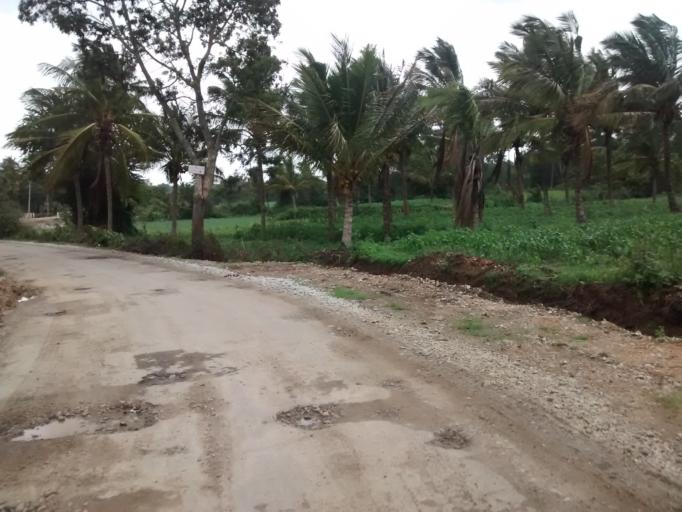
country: IN
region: Karnataka
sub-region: Hassan
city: Hassan
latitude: 12.9516
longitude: 76.1456
